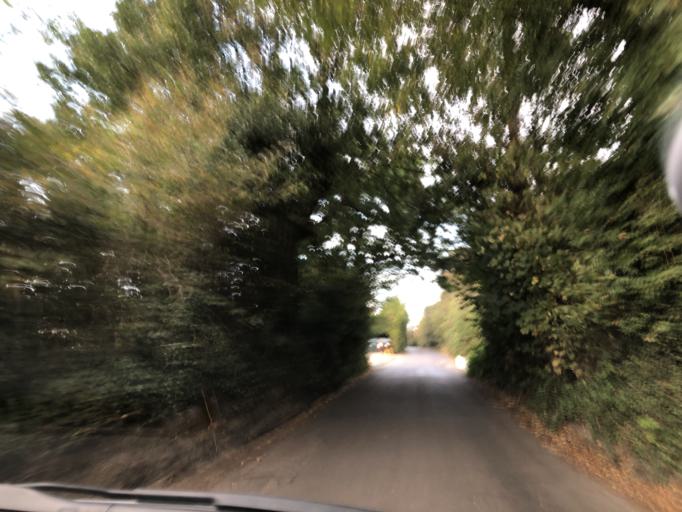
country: GB
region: England
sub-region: East Sussex
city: Bexhill-on-Sea
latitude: 50.8682
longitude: 0.4415
